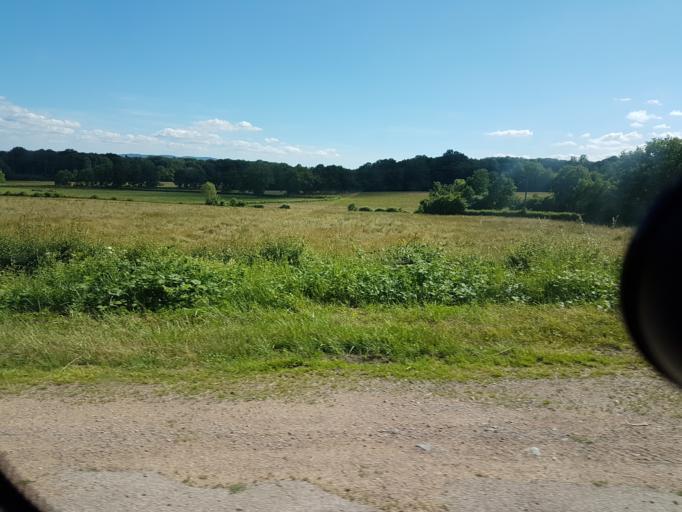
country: FR
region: Bourgogne
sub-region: Departement de Saone-et-Loire
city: Autun
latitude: 47.0529
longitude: 4.2891
